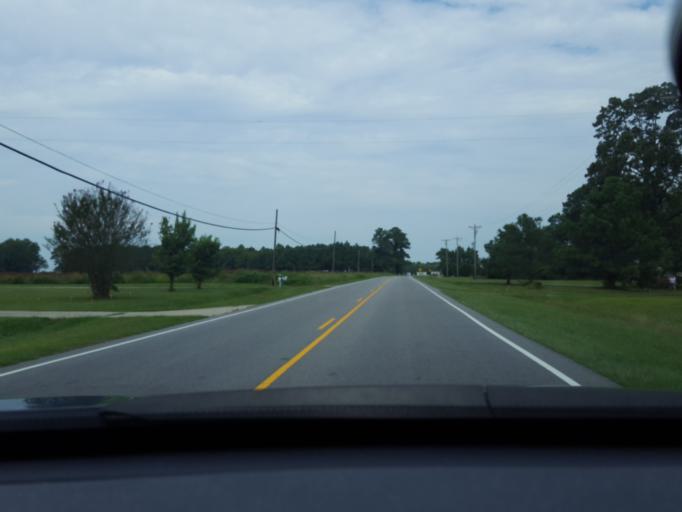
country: US
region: North Carolina
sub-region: Chowan County
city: Edenton
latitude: 36.1320
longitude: -76.6553
